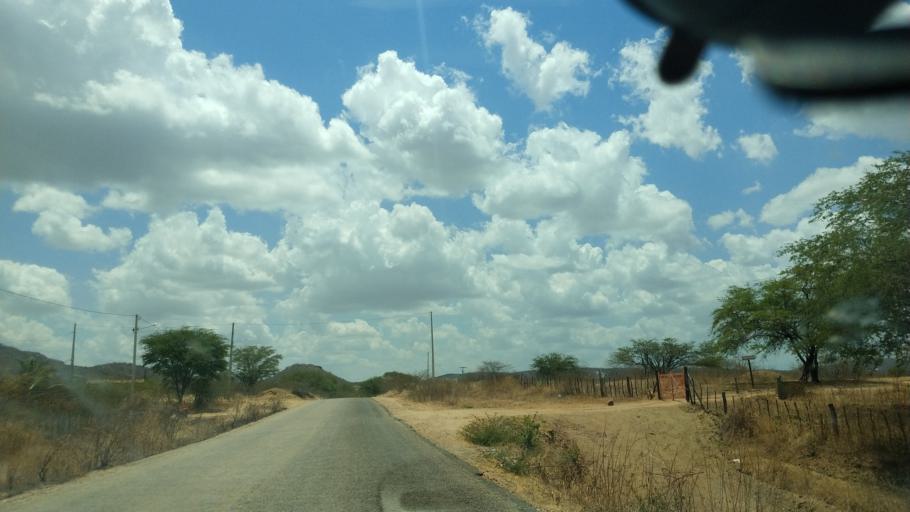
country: BR
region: Rio Grande do Norte
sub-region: Currais Novos
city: Currais Novos
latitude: -6.2739
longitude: -36.5455
